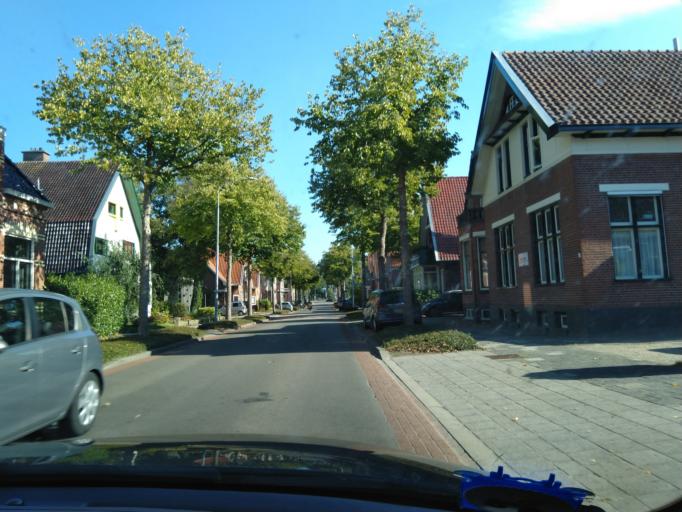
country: NL
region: Groningen
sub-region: Gemeente Veendam
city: Veendam
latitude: 53.0849
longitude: 6.8678
